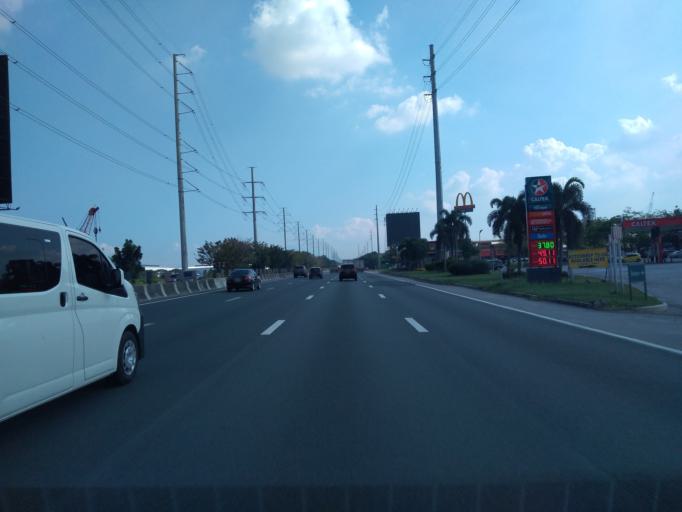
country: PH
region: Calabarzon
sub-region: Province of Laguna
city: Pulong Santa Cruz
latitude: 14.2982
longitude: 121.0818
